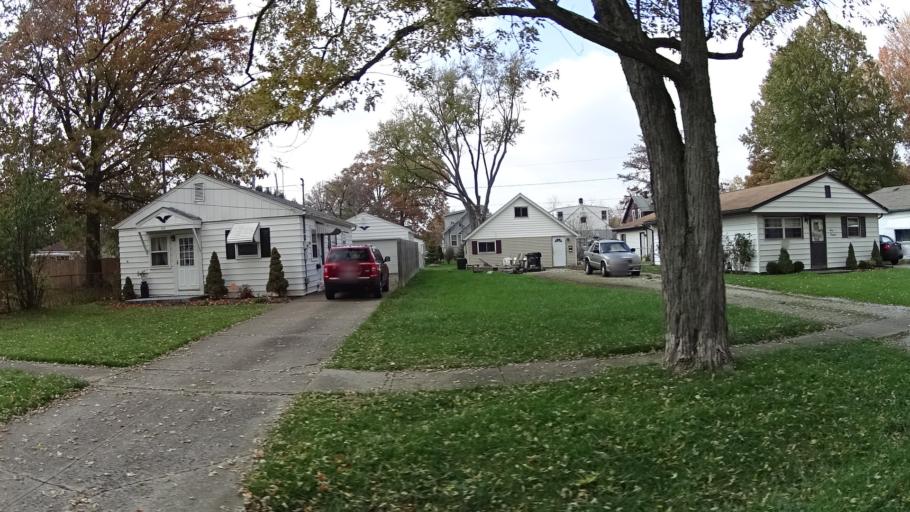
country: US
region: Ohio
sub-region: Lorain County
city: Elyria
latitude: 41.3821
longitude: -82.0825
